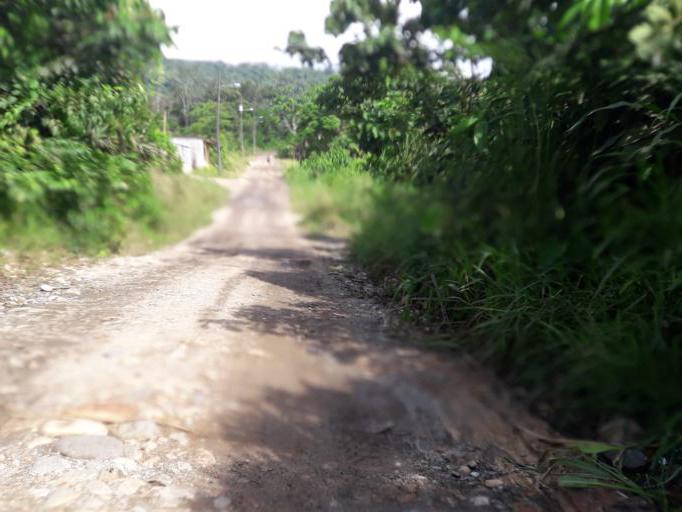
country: EC
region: Napo
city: Tena
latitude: -0.9562
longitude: -77.8177
